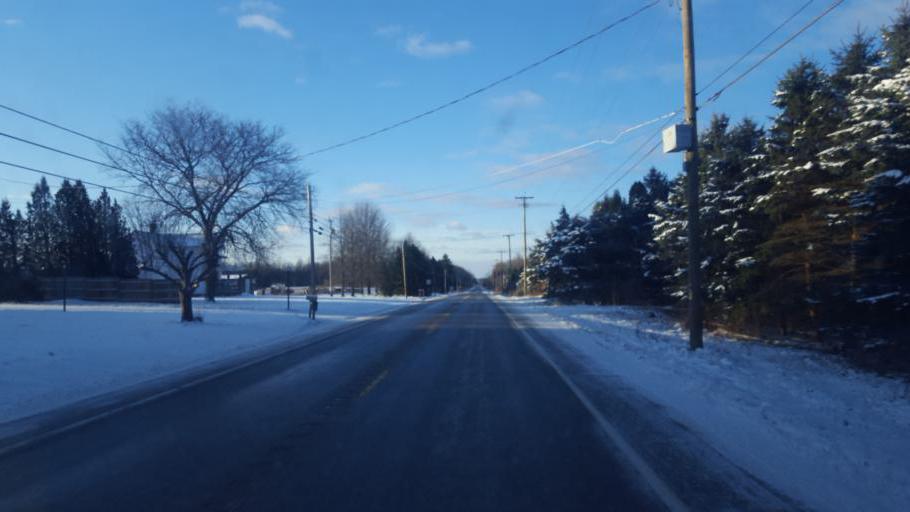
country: US
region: Pennsylvania
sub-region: Mercer County
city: Stoneboro
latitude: 41.3539
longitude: -80.2243
